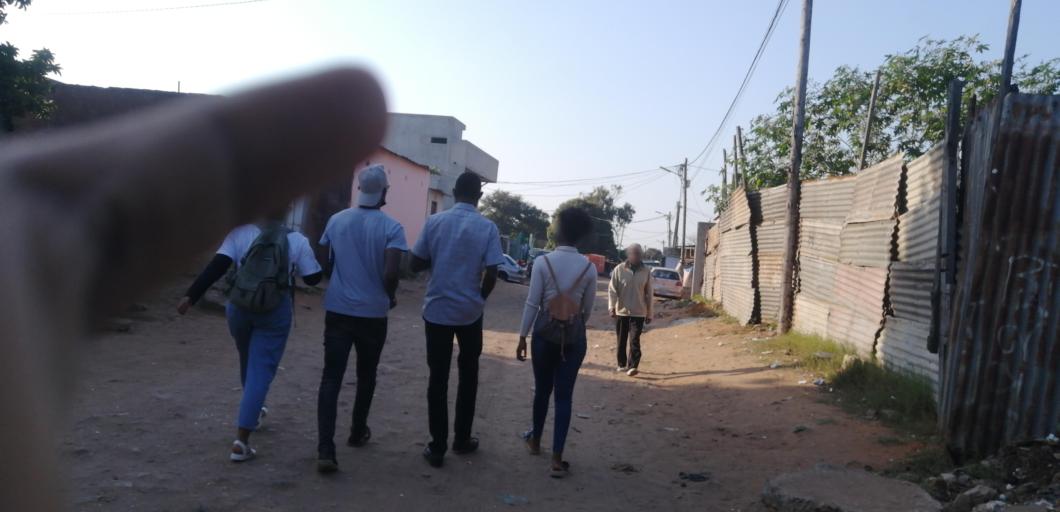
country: MZ
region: Maputo City
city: Maputo
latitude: -25.9551
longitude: 32.5686
